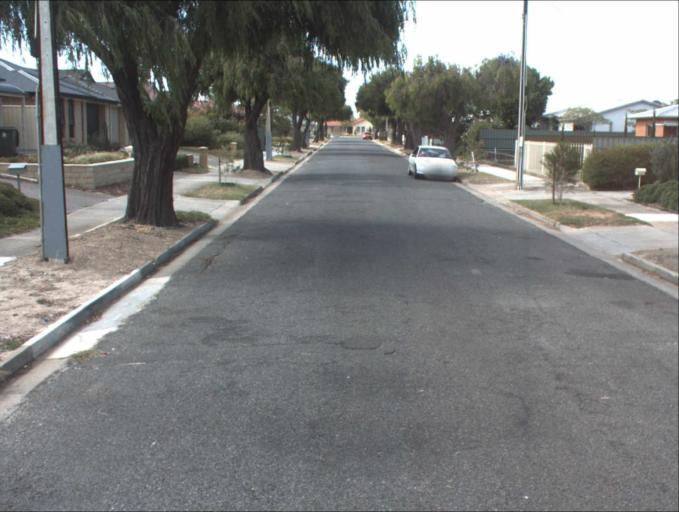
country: AU
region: South Australia
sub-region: Port Adelaide Enfield
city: Birkenhead
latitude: -34.7996
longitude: 138.4948
